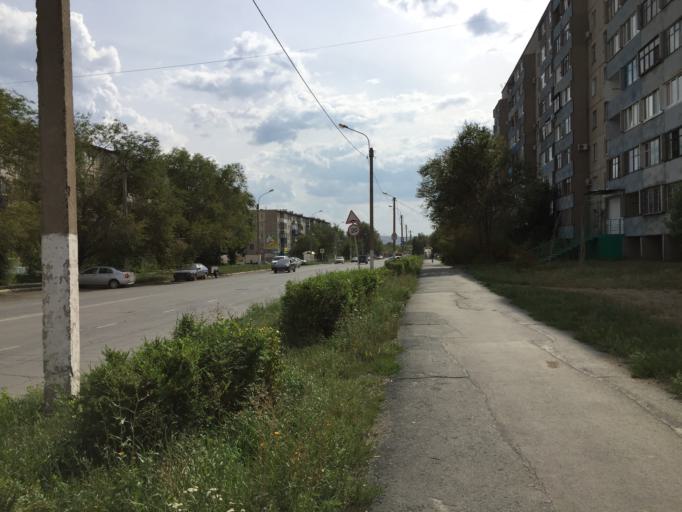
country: RU
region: Orenburg
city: Novotroitsk
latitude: 51.1843
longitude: 58.2769
